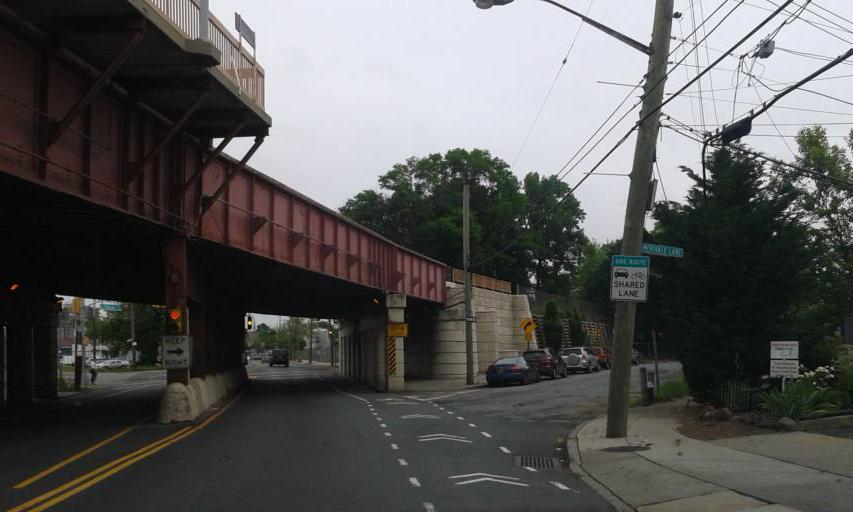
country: US
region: New Jersey
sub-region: Hudson County
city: Bayonne
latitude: 40.6211
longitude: -74.0715
